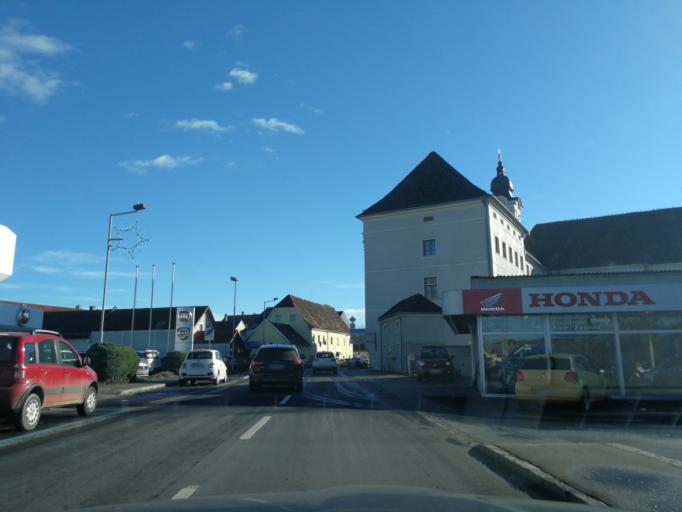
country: AT
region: Styria
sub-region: Politischer Bezirk Weiz
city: Gleisdorf
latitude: 47.1048
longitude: 15.7039
